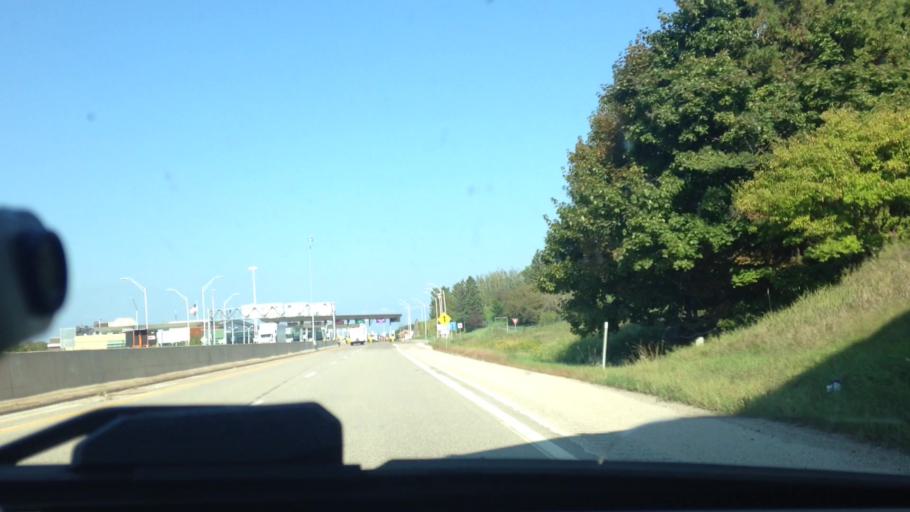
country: US
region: Michigan
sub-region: Chippewa County
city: Sault Ste. Marie
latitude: 46.4918
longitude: -84.3707
